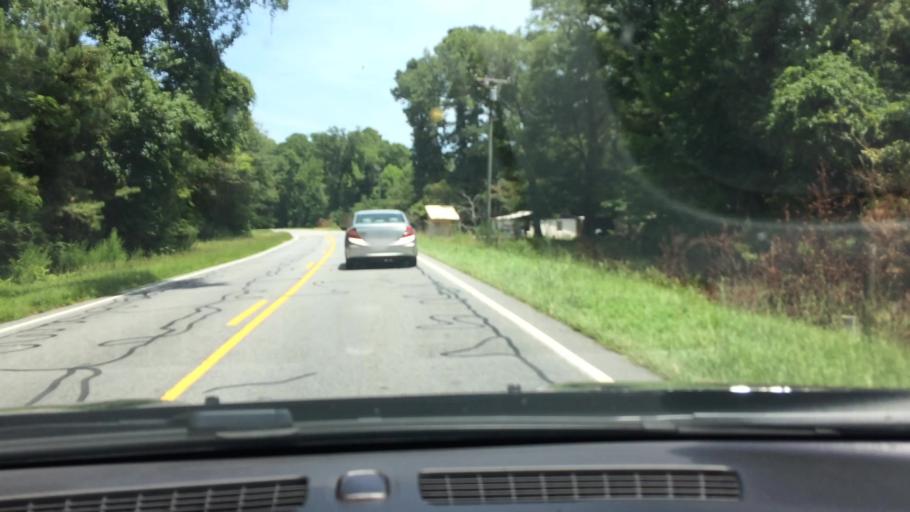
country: US
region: North Carolina
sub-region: Beaufort County
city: Washington
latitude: 35.5854
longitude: -77.1672
